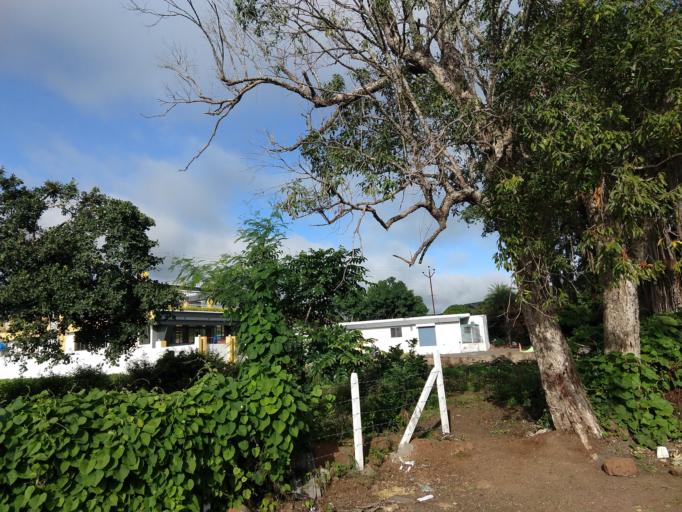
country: IN
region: Maharashtra
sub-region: Pune Division
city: Khed
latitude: 18.3938
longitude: 73.9196
